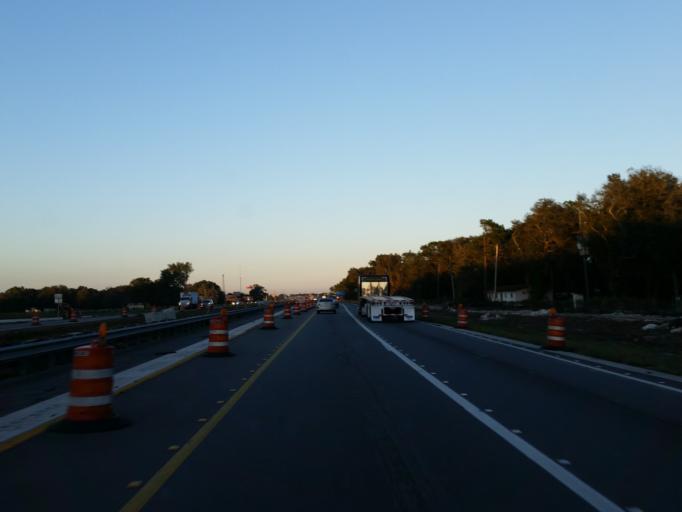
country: US
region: Florida
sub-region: Sumter County
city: Bushnell
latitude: 28.6588
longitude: -82.1494
